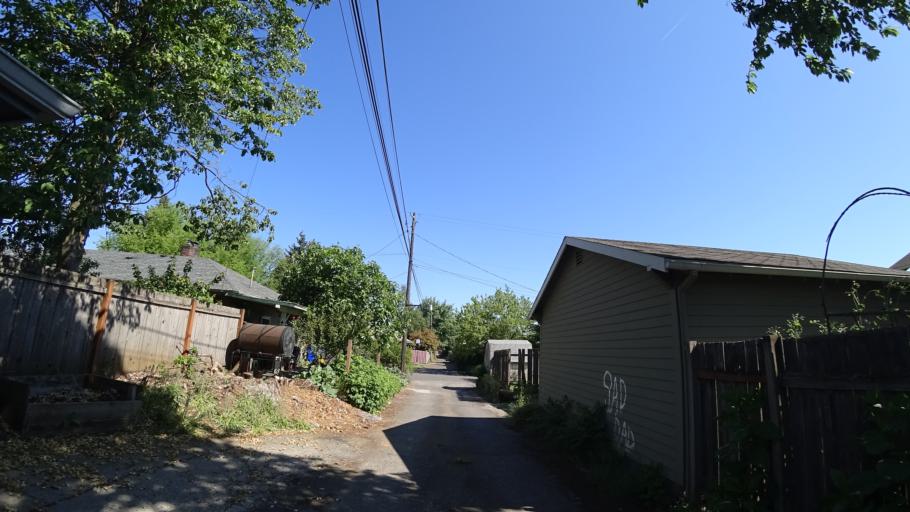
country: US
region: Oregon
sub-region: Multnomah County
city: Portland
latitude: 45.5686
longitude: -122.6632
